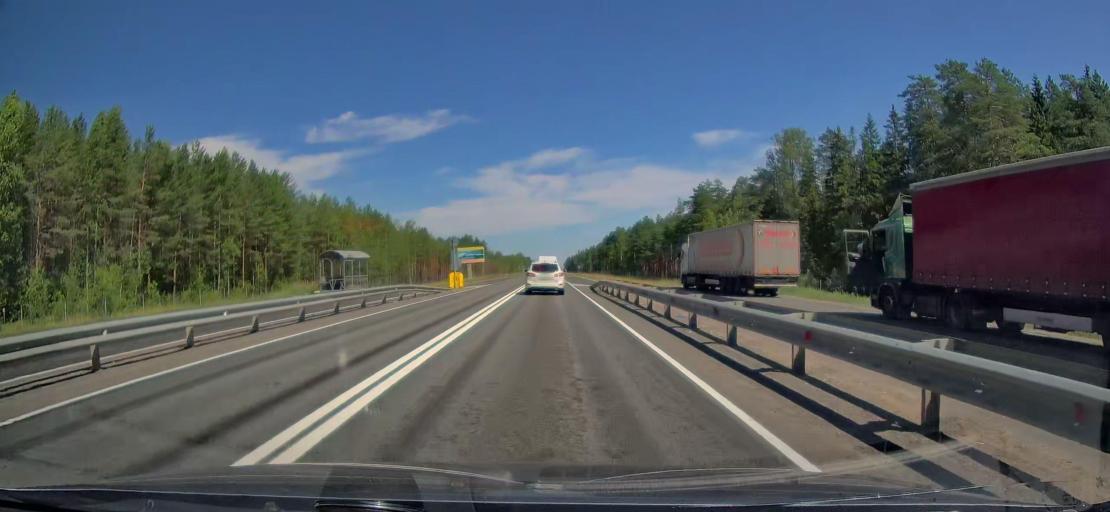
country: RU
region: Vologda
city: Khokhlovo
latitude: 58.9637
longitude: 37.3072
